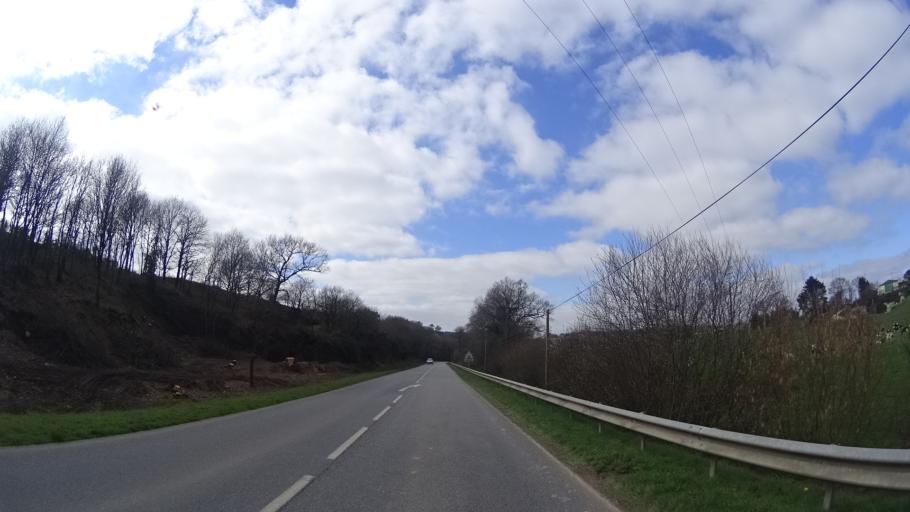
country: FR
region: Brittany
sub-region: Departement du Morbihan
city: Ruffiac
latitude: 47.8296
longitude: -2.3053
